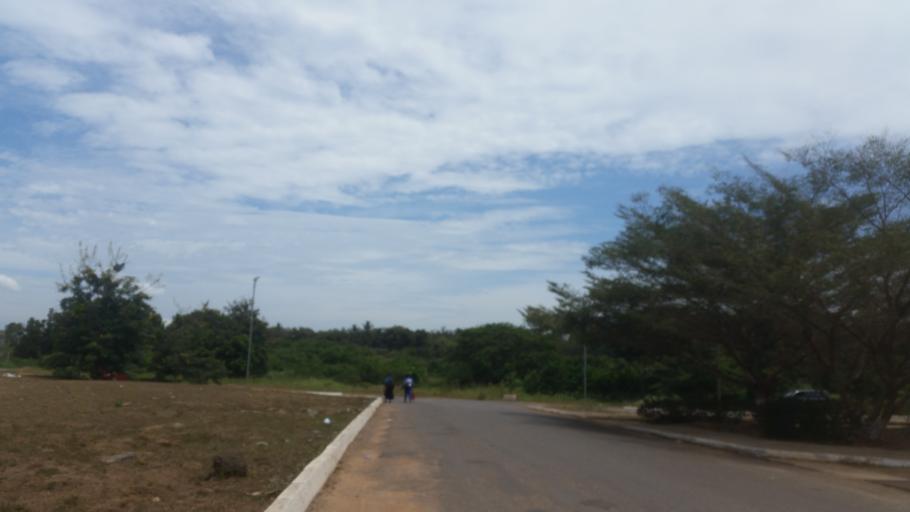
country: GH
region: Central
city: Cape Coast
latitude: 5.1199
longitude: -1.2929
